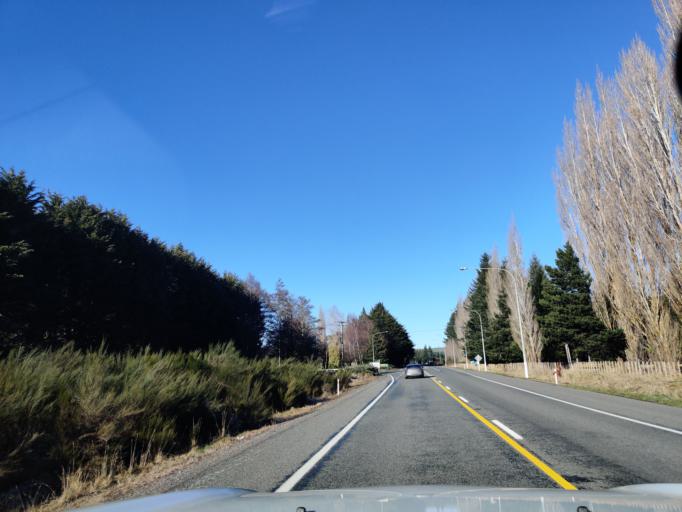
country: NZ
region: Manawatu-Wanganui
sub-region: Ruapehu District
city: Waiouru
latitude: -39.4665
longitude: 175.6723
